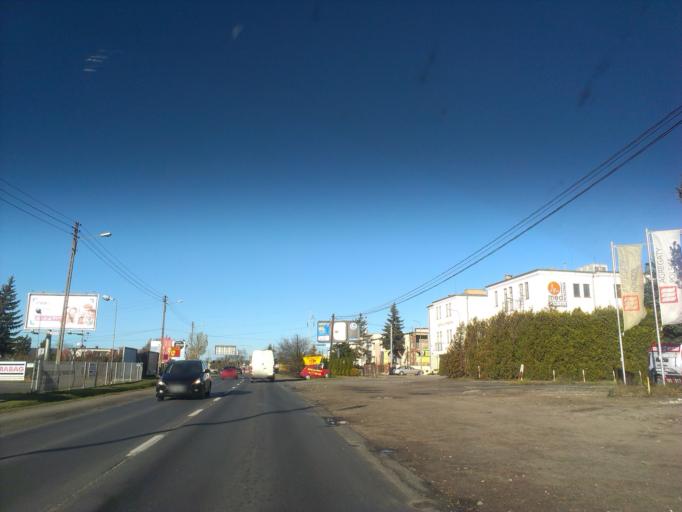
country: PL
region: Greater Poland Voivodeship
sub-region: Powiat poznanski
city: Suchy Las
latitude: 52.4473
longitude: 16.9078
